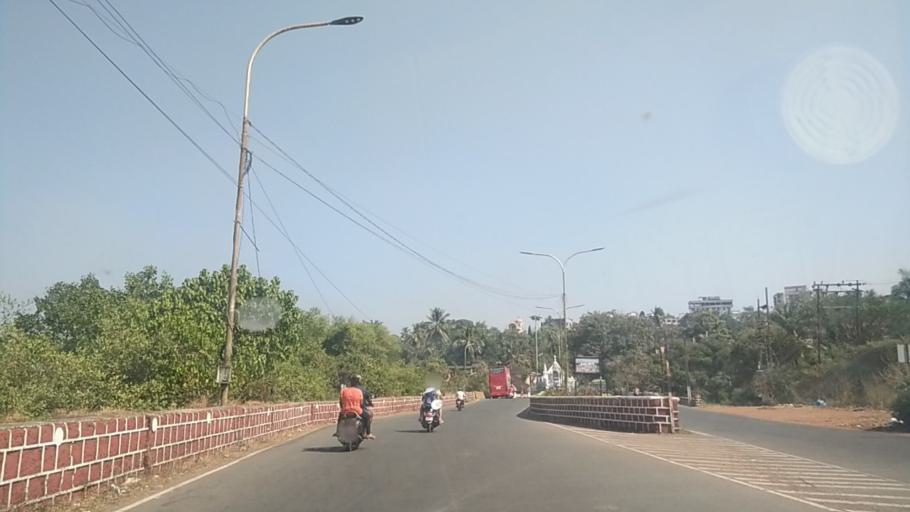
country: IN
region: Goa
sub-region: North Goa
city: Panaji
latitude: 15.5036
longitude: 73.8610
